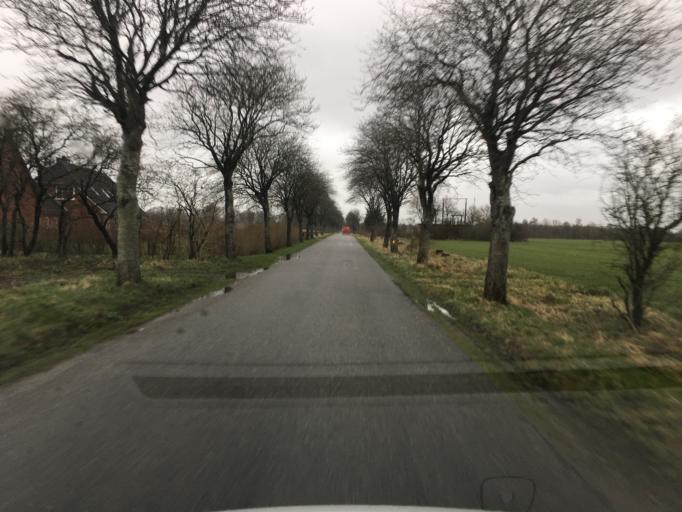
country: DK
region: South Denmark
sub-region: Aabenraa Kommune
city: Tinglev
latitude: 54.9022
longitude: 9.3045
